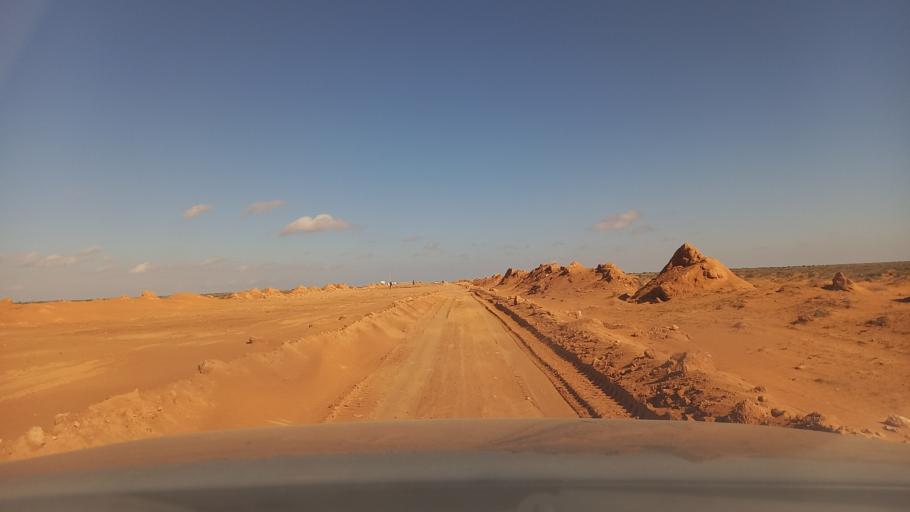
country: TN
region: Madanin
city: Medenine
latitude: 33.2451
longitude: 10.5600
